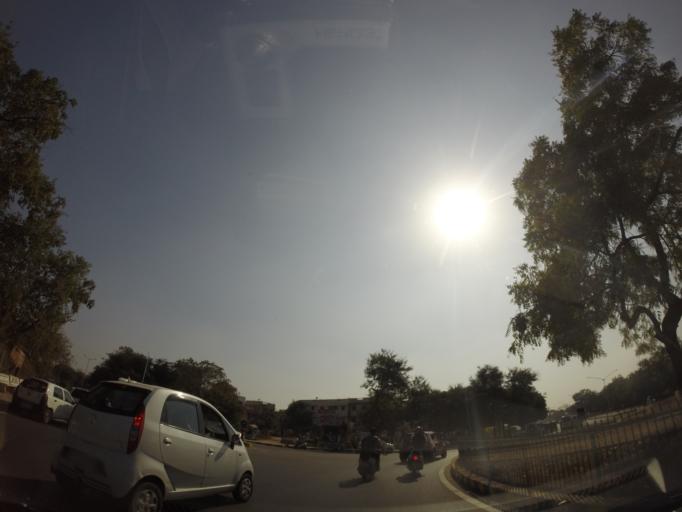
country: IN
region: Gujarat
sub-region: Gandhinagar
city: Ghandinagar
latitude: 23.2082
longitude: 72.6361
